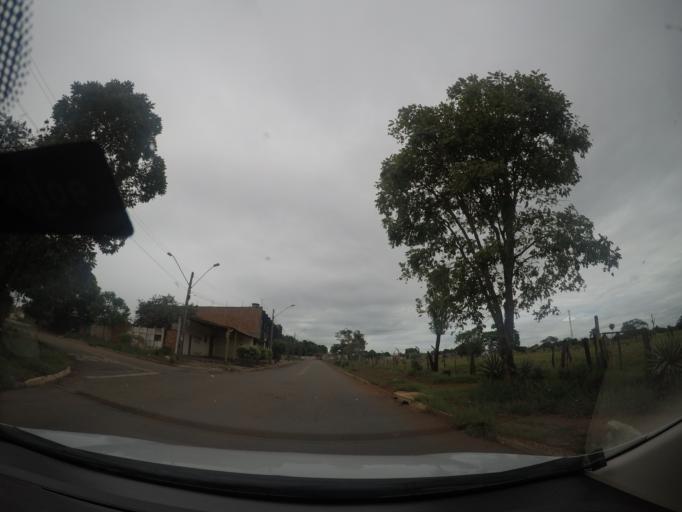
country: BR
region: Goias
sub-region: Goiania
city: Goiania
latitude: -16.6136
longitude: -49.3504
